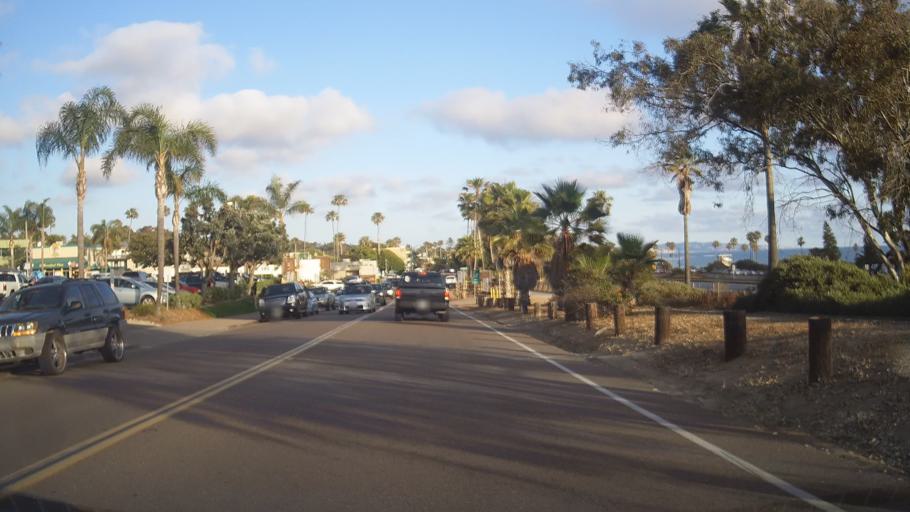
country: US
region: California
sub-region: San Diego County
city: Encinitas
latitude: 33.0220
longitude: -117.2830
